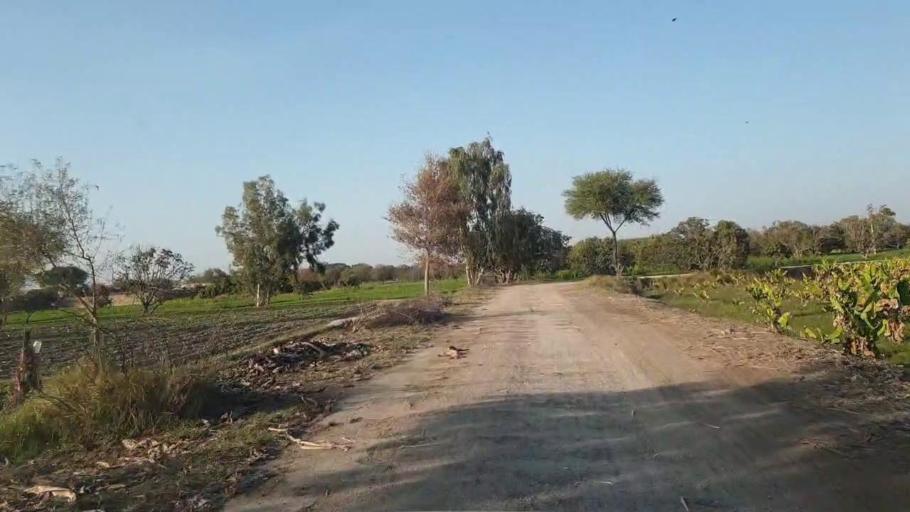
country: PK
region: Sindh
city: Tando Allahyar
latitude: 25.3766
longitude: 68.7014
